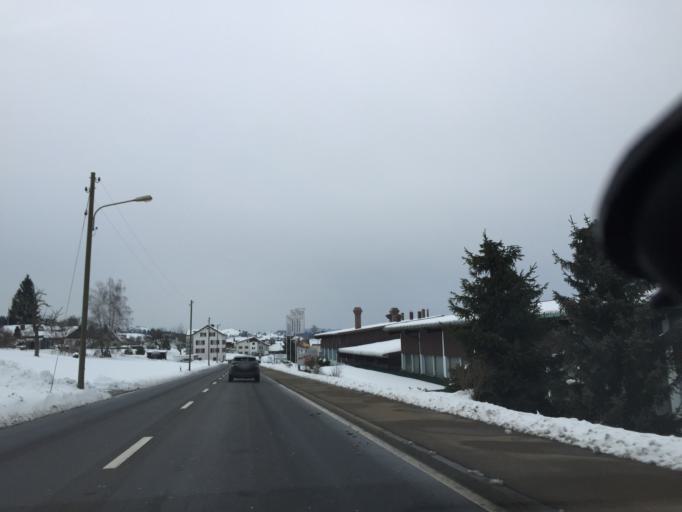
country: CH
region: Zurich
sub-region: Bezirk Horgen
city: Richterswil / Burghalde
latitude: 47.1878
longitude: 8.6808
